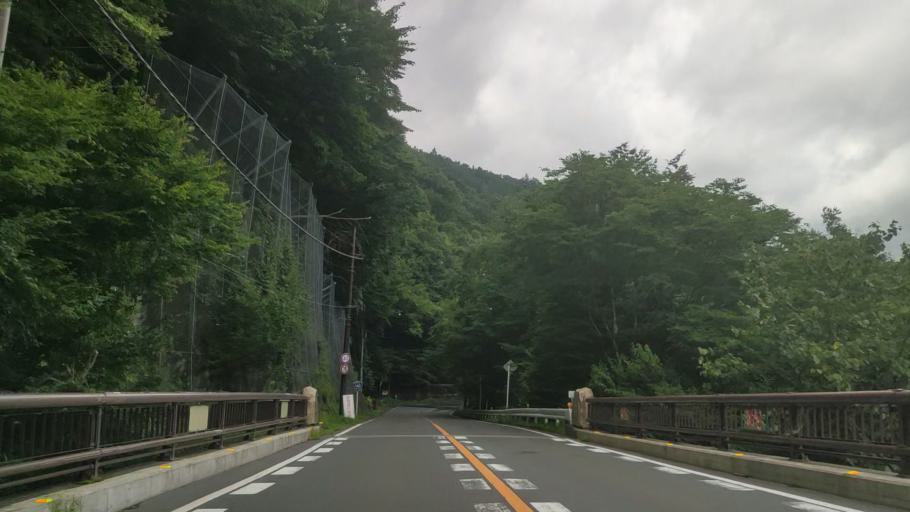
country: JP
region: Yamanashi
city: Enzan
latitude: 35.9169
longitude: 138.8311
